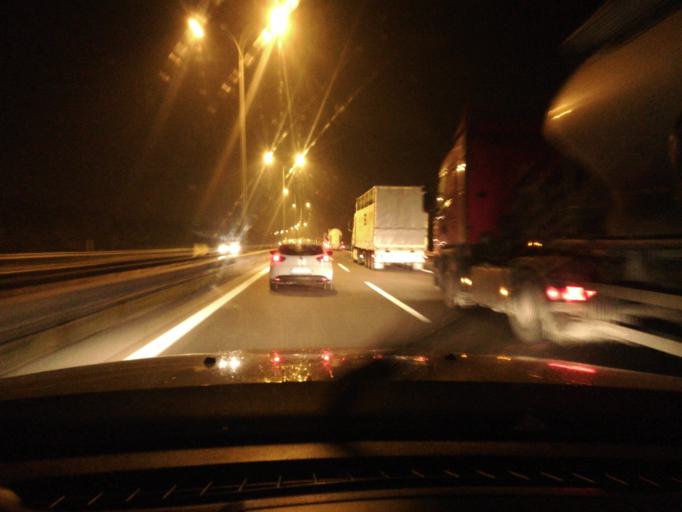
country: TR
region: Istanbul
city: Celaliye
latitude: 41.0626
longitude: 28.4073
